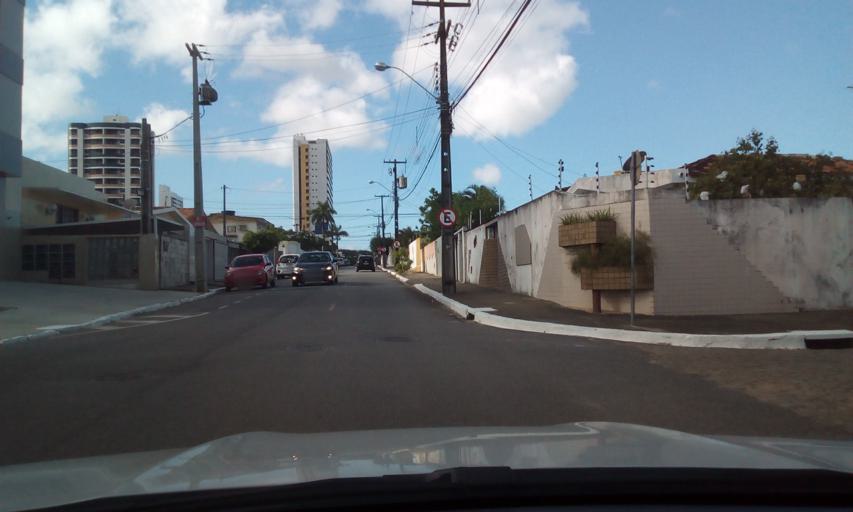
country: BR
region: Paraiba
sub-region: Joao Pessoa
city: Joao Pessoa
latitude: -7.1237
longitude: -34.8470
